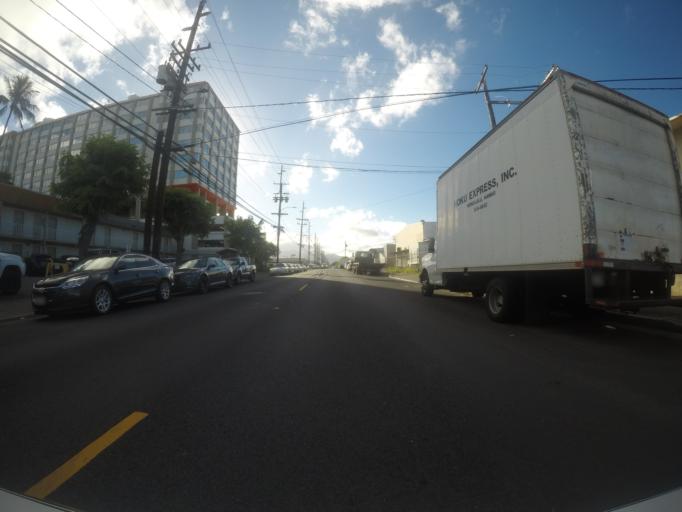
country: US
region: Hawaii
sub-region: Honolulu County
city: Halawa Heights
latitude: 21.3358
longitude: -157.9138
